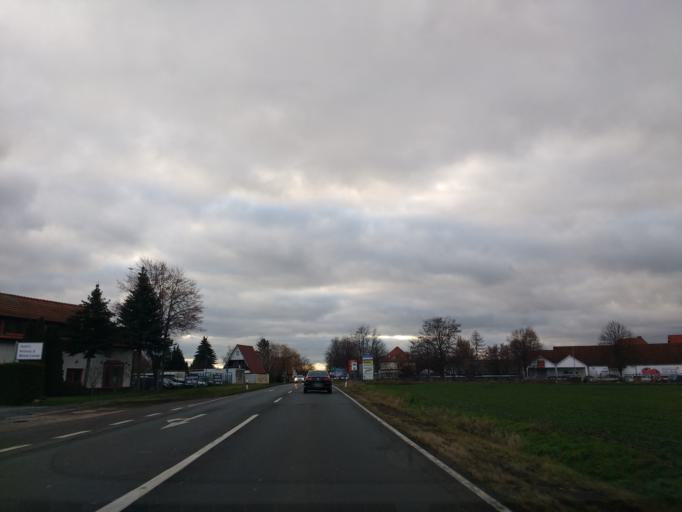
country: DE
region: Saxony-Anhalt
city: Braunsbedra
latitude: 51.2887
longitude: 11.9044
